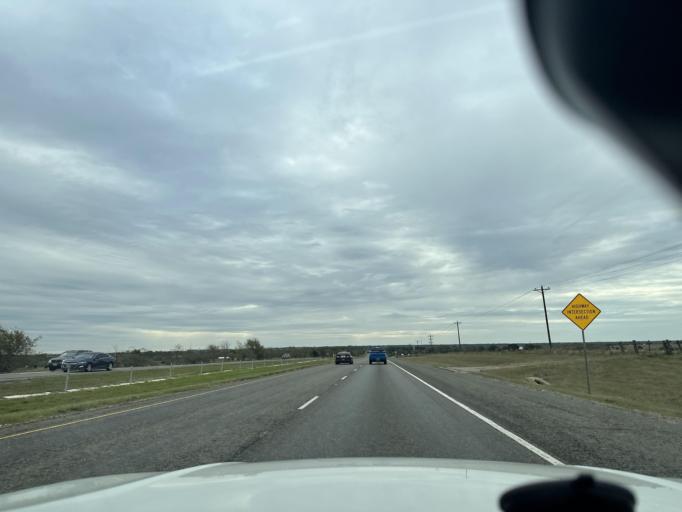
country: US
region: Texas
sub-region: Burleson County
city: Somerville
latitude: 30.1886
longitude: -96.5567
